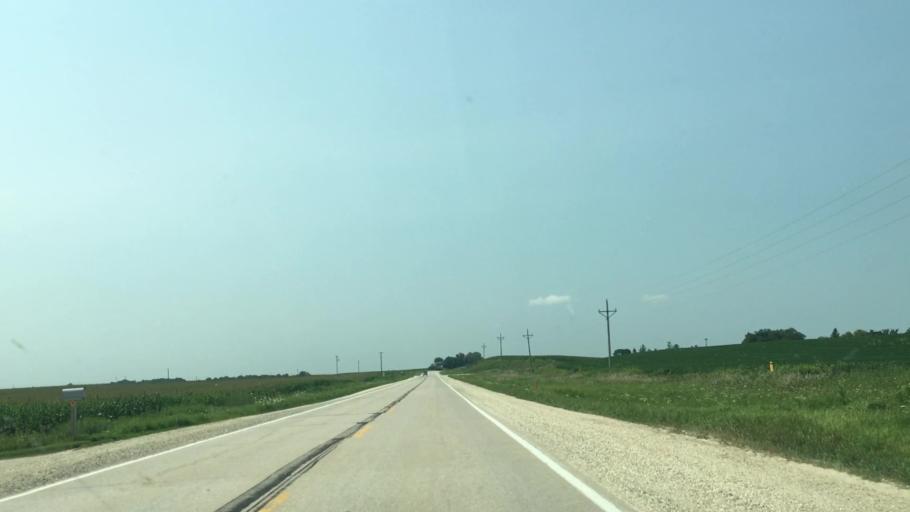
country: US
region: Iowa
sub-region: Fayette County
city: West Union
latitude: 43.0947
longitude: -91.8601
